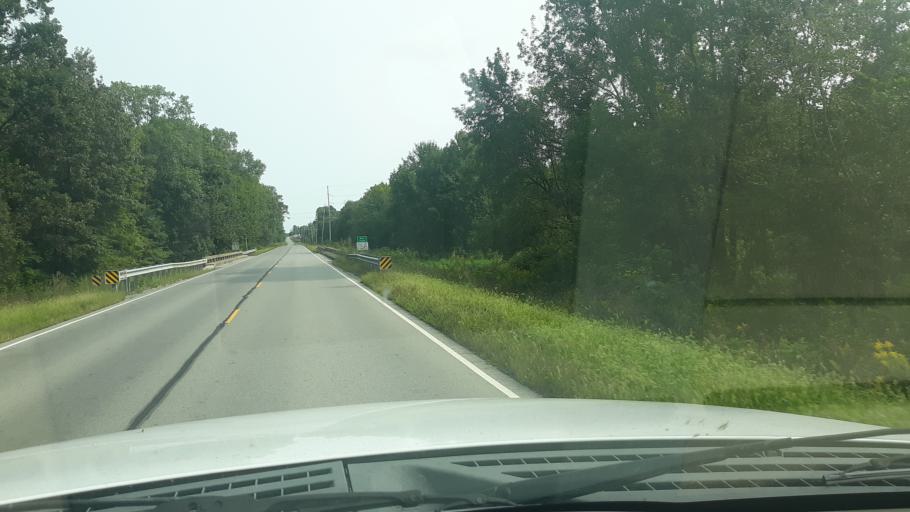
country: US
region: Illinois
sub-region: White County
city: Norris City
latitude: 37.9414
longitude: -88.3428
